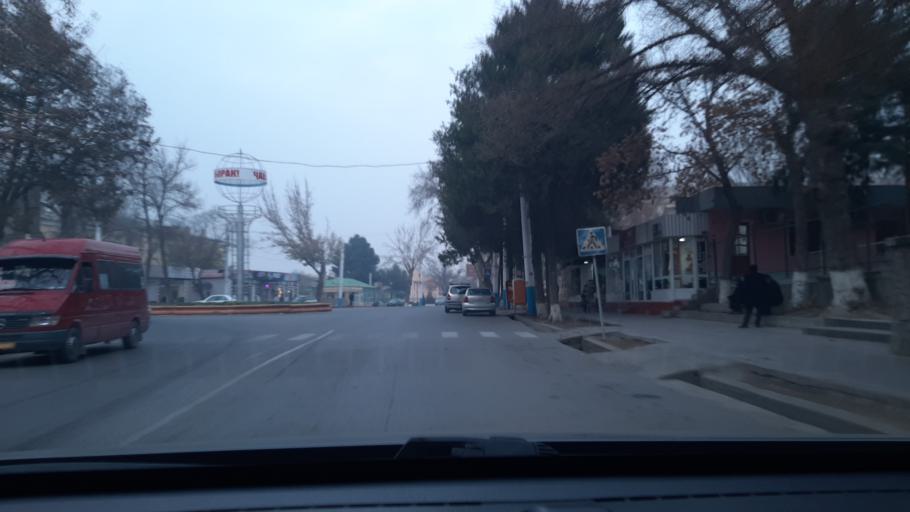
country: TJ
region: Viloyati Sughd
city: Khujand
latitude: 40.2731
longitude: 69.6059
